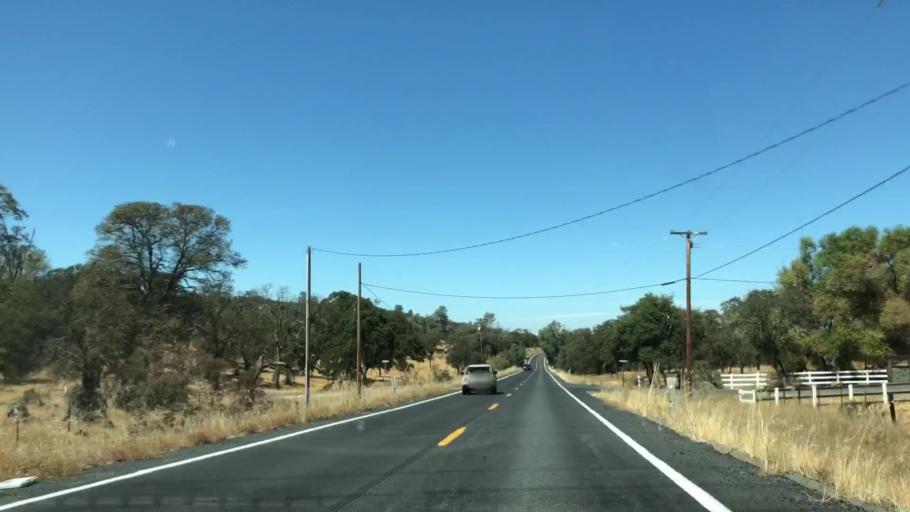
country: US
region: California
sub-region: Calaveras County
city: Copperopolis
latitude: 37.8899
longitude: -120.5451
